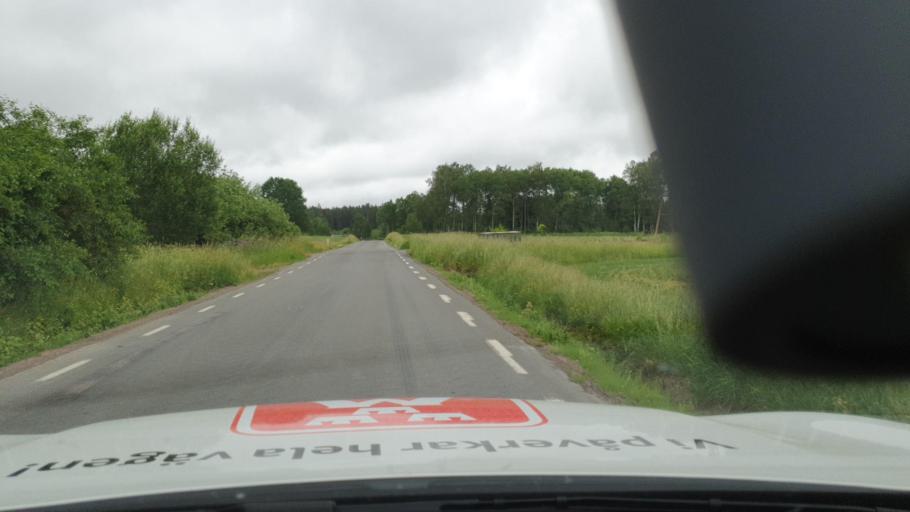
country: SE
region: Vaestra Goetaland
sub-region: Tibro Kommun
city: Tibro
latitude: 58.4065
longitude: 14.0641
